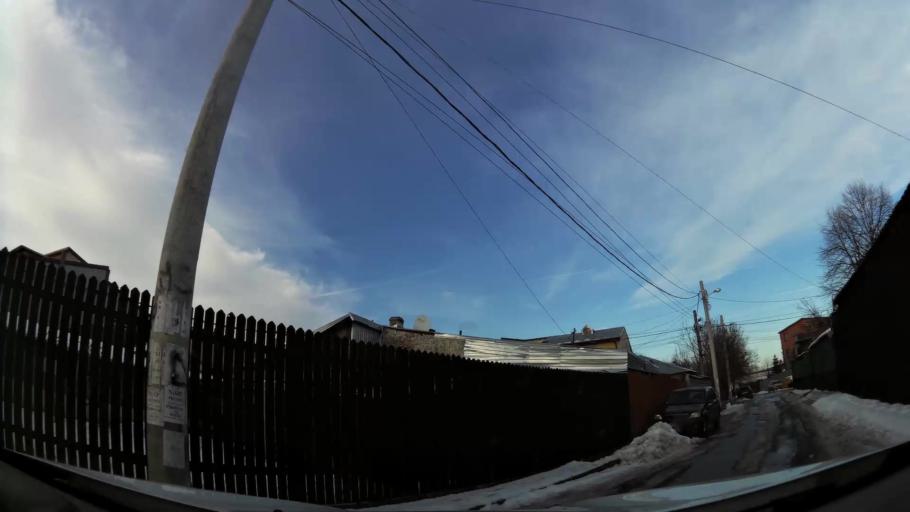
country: RO
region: Bucuresti
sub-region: Municipiul Bucuresti
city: Bucuresti
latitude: 44.3872
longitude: 26.0761
